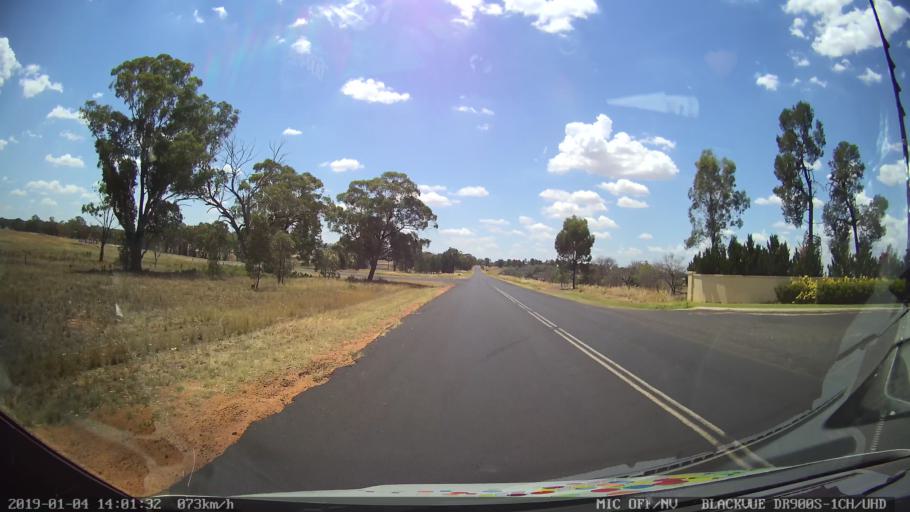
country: AU
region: New South Wales
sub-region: Dubbo Municipality
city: Dubbo
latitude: -32.2957
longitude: 148.5991
